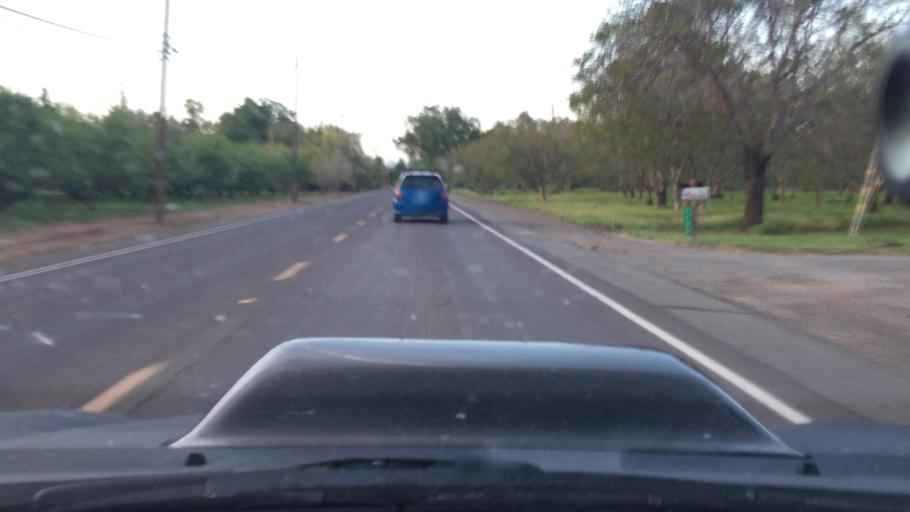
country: US
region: California
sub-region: Butte County
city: Chico
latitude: 39.7086
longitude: -121.8461
